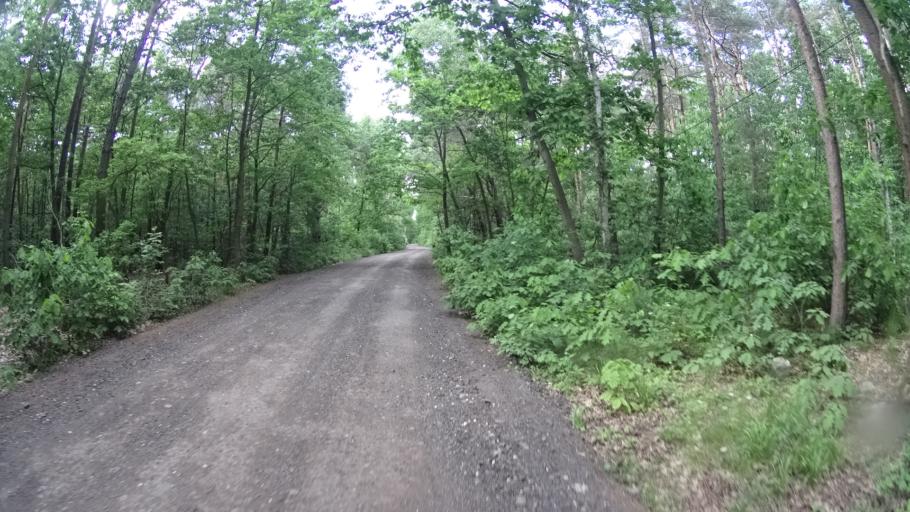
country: PL
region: Masovian Voivodeship
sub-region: Powiat pruszkowski
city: Nadarzyn
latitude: 52.0630
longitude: 20.8214
